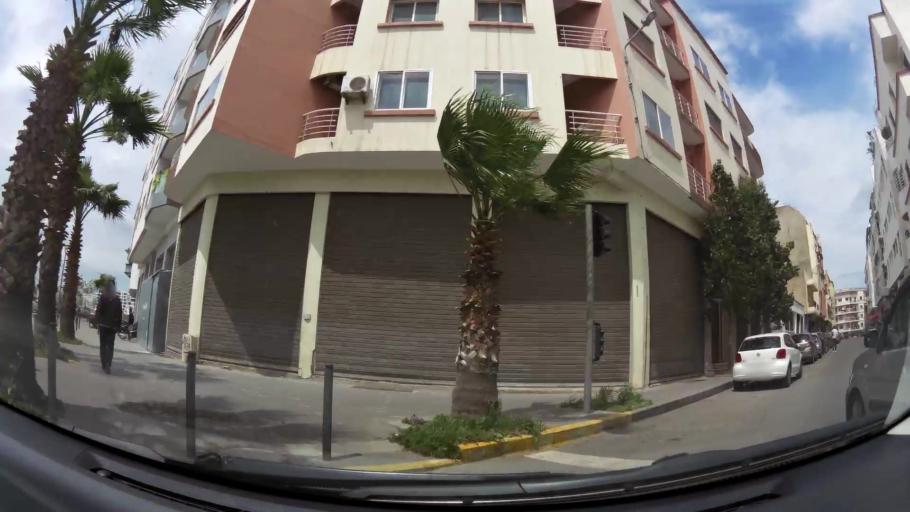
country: MA
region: Grand Casablanca
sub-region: Casablanca
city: Casablanca
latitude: 33.5662
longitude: -7.6543
